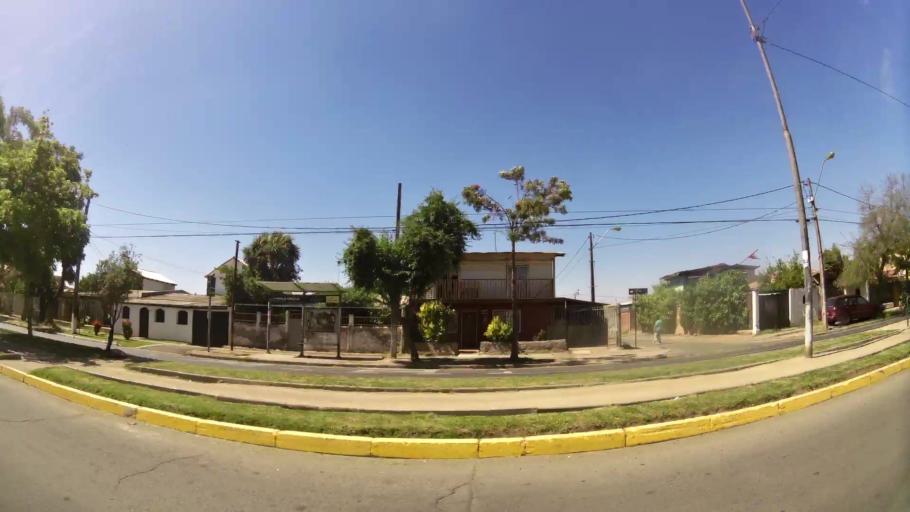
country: CL
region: Santiago Metropolitan
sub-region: Provincia de Maipo
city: San Bernardo
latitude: -33.5769
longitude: -70.6821
